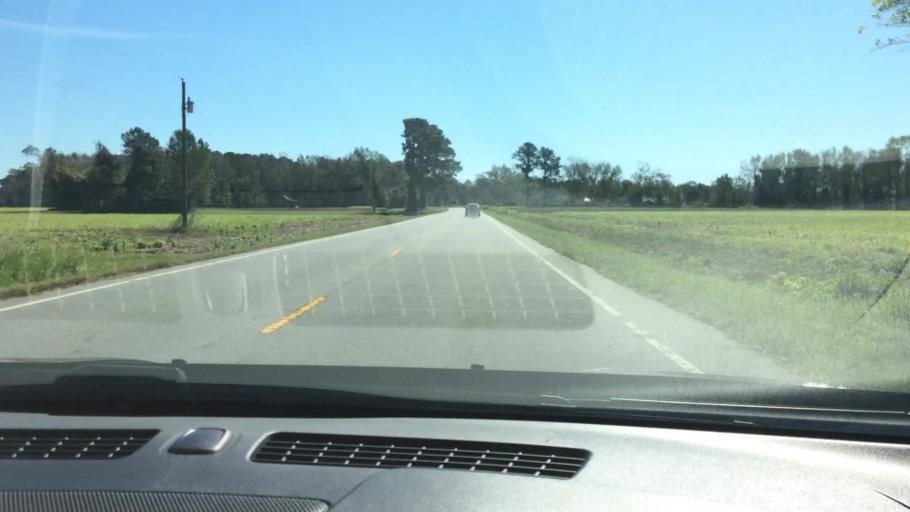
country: US
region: North Carolina
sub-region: Pitt County
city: Grifton
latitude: 35.3586
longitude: -77.3428
